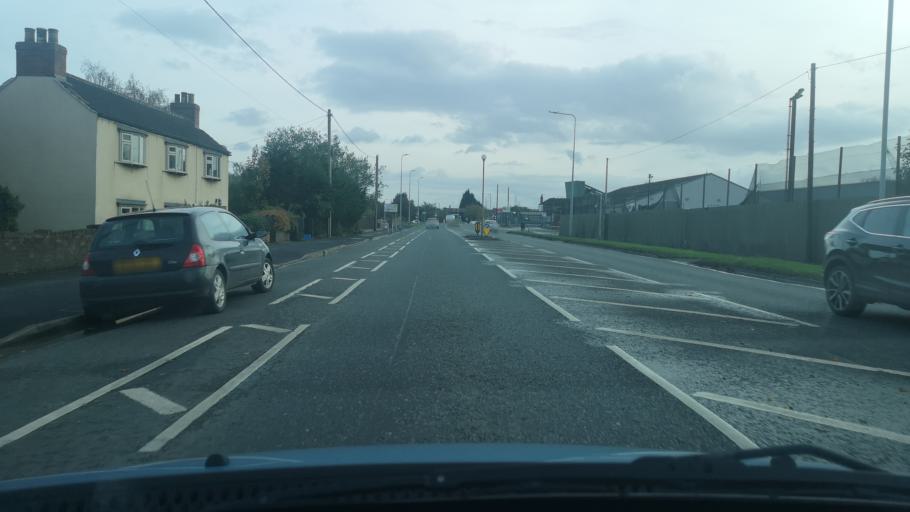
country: GB
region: England
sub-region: North Lincolnshire
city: Gunness
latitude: 53.5893
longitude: -0.7285
